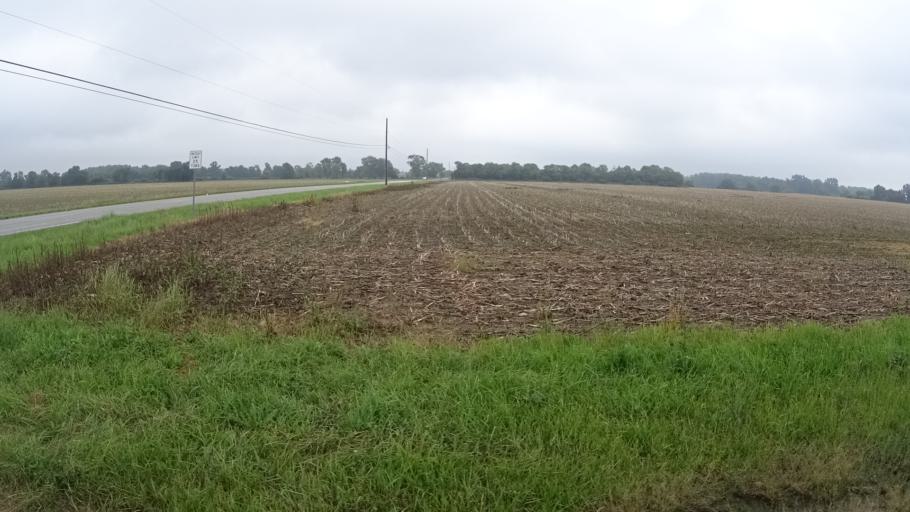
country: US
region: Ohio
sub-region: Huron County
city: Bellevue
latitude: 41.3621
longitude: -82.8173
